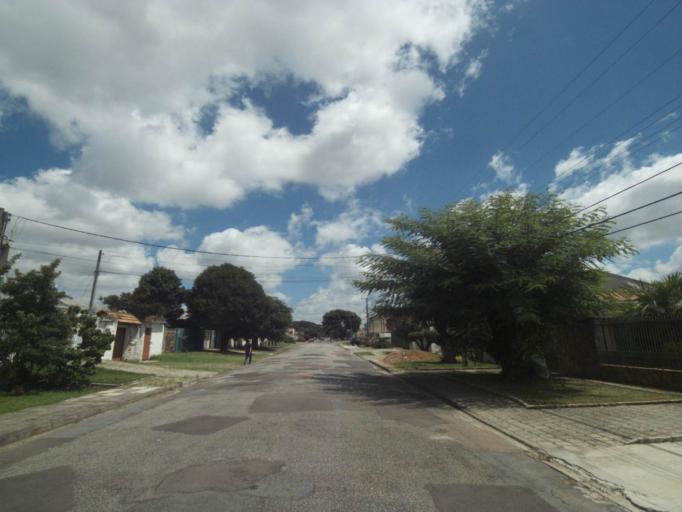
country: BR
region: Parana
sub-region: Pinhais
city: Pinhais
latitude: -25.4380
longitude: -49.2124
